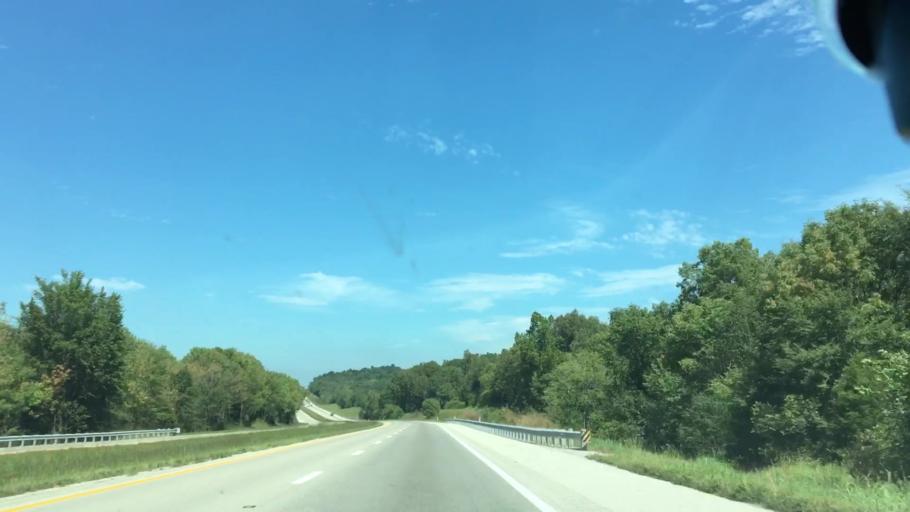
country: US
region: Kentucky
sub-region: Christian County
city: Hopkinsville
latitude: 36.9285
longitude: -87.4708
